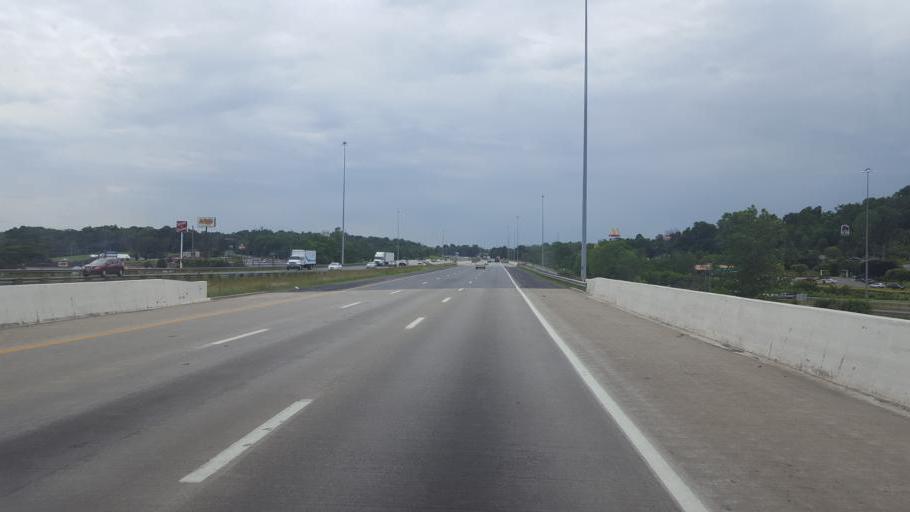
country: US
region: Ohio
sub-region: Richland County
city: Mansfield
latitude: 40.6964
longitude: -82.5092
